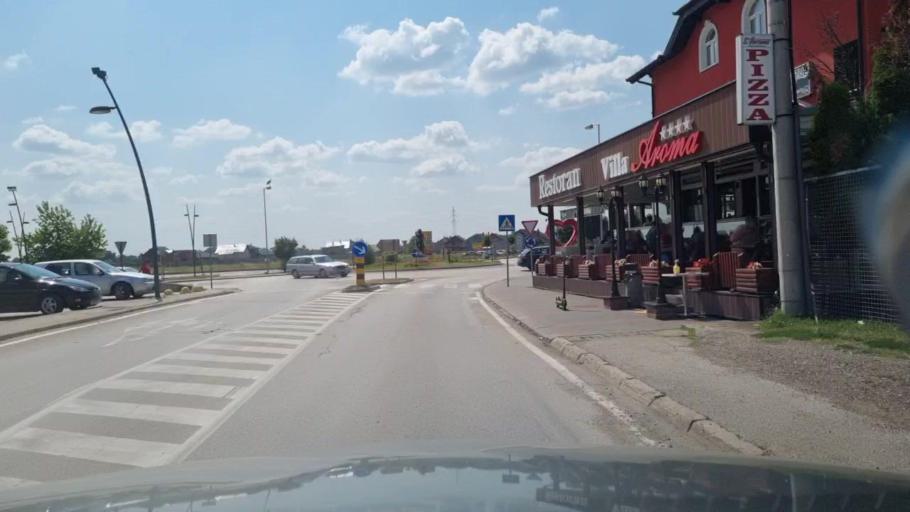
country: BA
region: Federation of Bosnia and Herzegovina
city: Orasje
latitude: 45.0263
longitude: 18.6996
